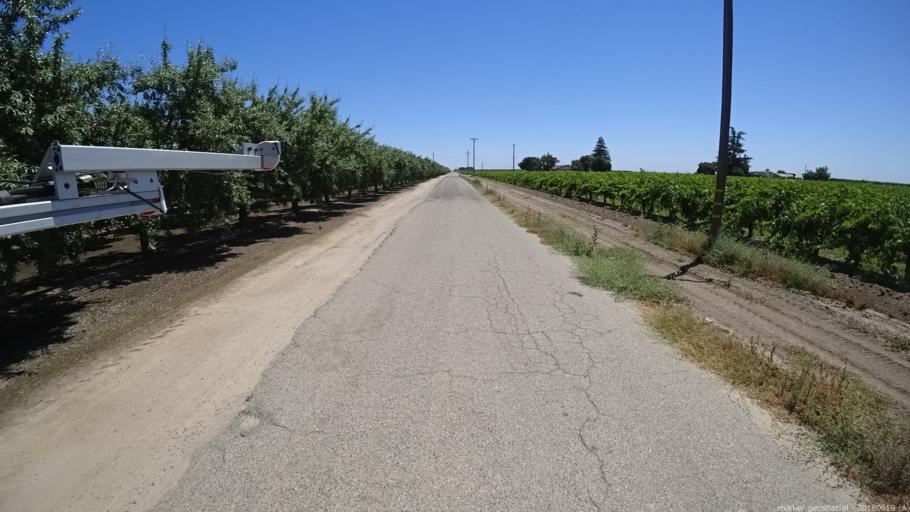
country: US
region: California
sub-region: Madera County
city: Parkwood
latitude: 36.8730
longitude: -120.1054
